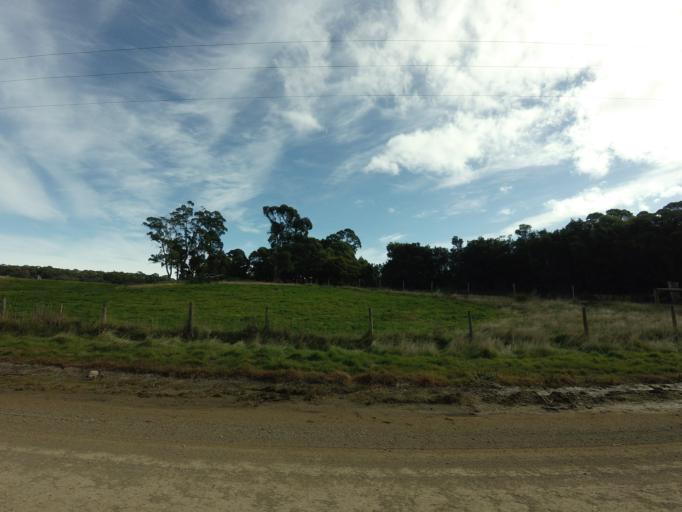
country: AU
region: Tasmania
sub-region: Clarence
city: Sandford
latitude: -43.1644
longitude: 147.7683
